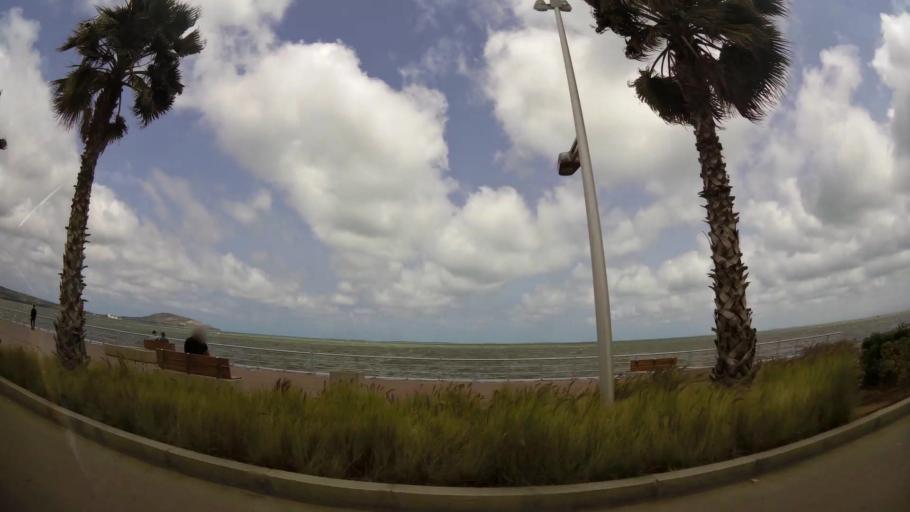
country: MA
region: Oriental
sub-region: Nador
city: Nador
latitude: 35.1780
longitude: -2.9206
